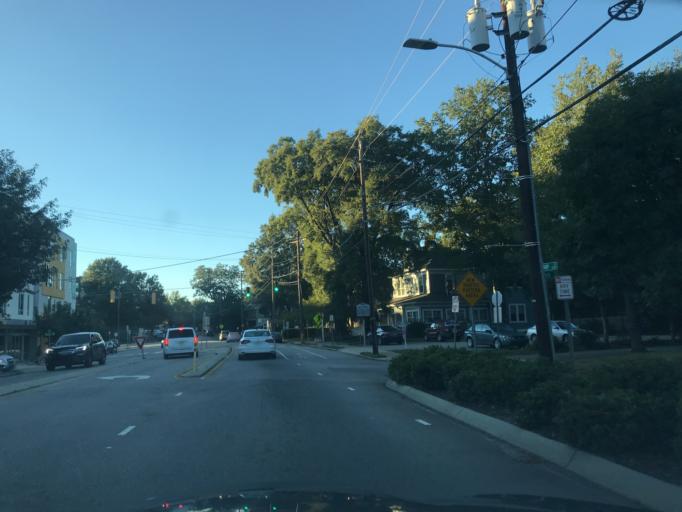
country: US
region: North Carolina
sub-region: Wake County
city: West Raleigh
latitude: 35.7829
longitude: -78.6555
